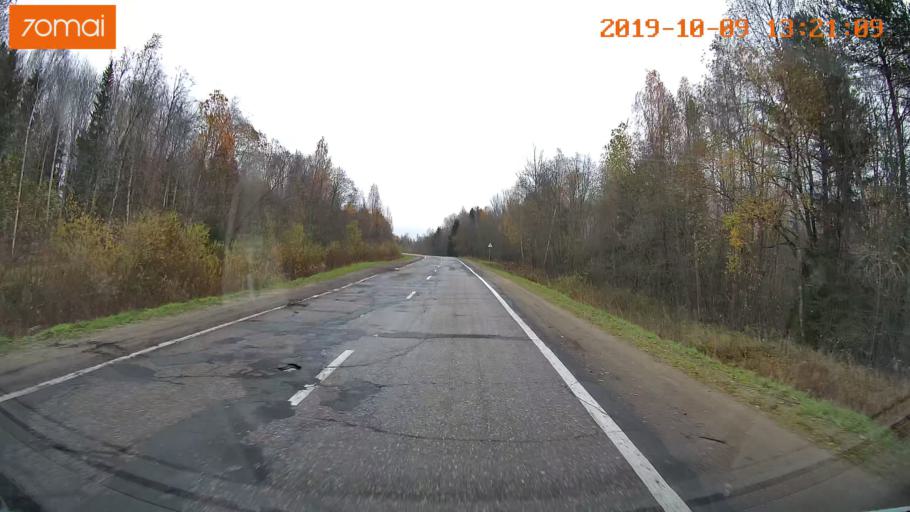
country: RU
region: Jaroslavl
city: Lyubim
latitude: 58.3409
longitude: 40.8413
